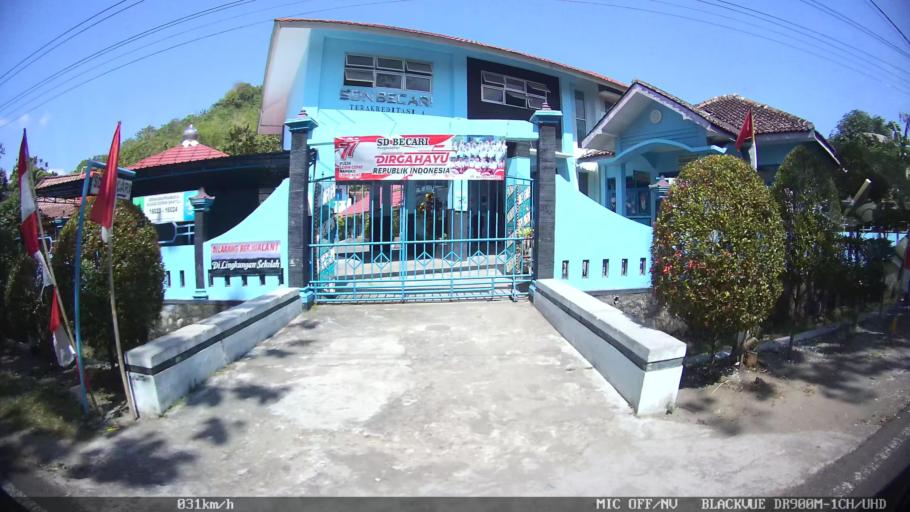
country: ID
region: Daerah Istimewa Yogyakarta
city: Pundong
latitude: -7.9596
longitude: 110.3583
